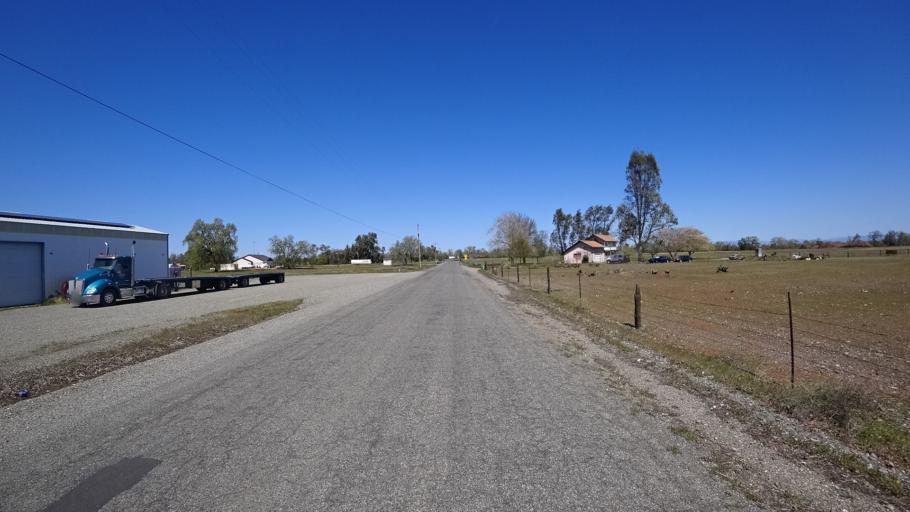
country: US
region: California
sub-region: Glenn County
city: Orland
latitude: 39.7744
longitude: -122.2297
